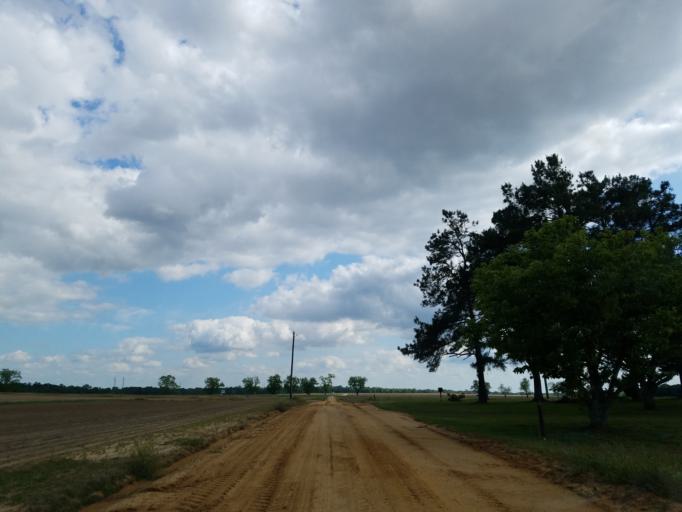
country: US
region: Georgia
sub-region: Dooly County
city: Vienna
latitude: 32.1708
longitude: -83.7759
